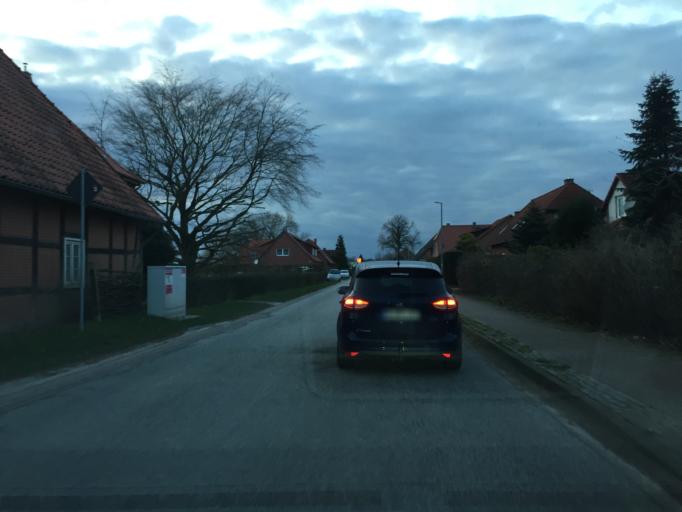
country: DE
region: Lower Saxony
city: Neustadt am Rubenberge
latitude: 52.5751
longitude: 9.4205
